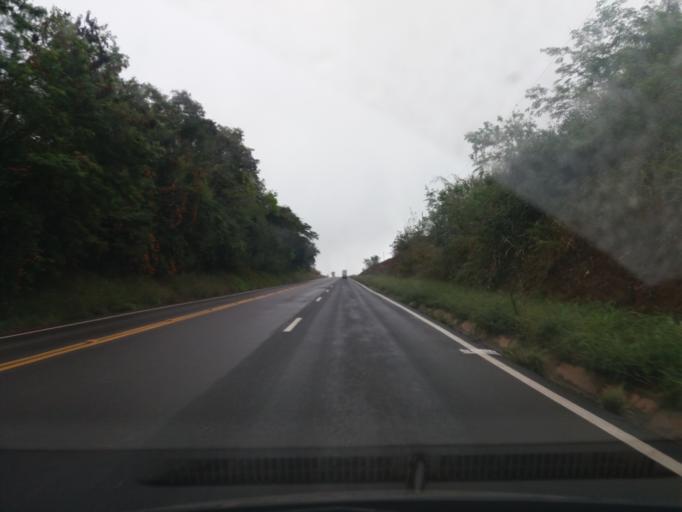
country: BR
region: Parana
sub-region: Realeza
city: Realeza
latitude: -25.5579
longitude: -53.5840
